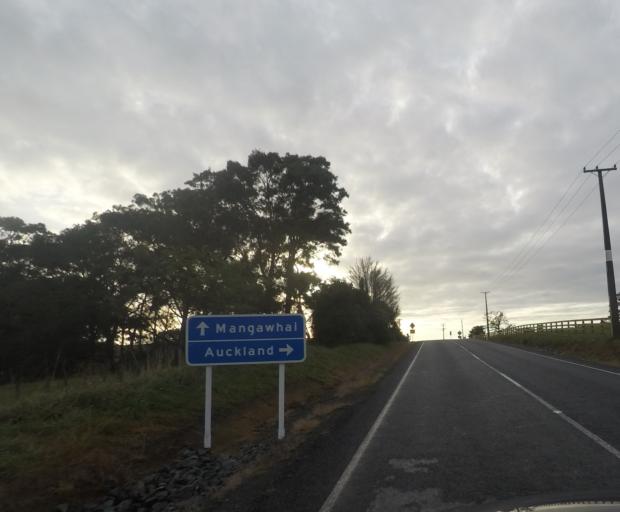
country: NZ
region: Auckland
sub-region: Auckland
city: Wellsford
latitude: -36.2226
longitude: 174.5741
